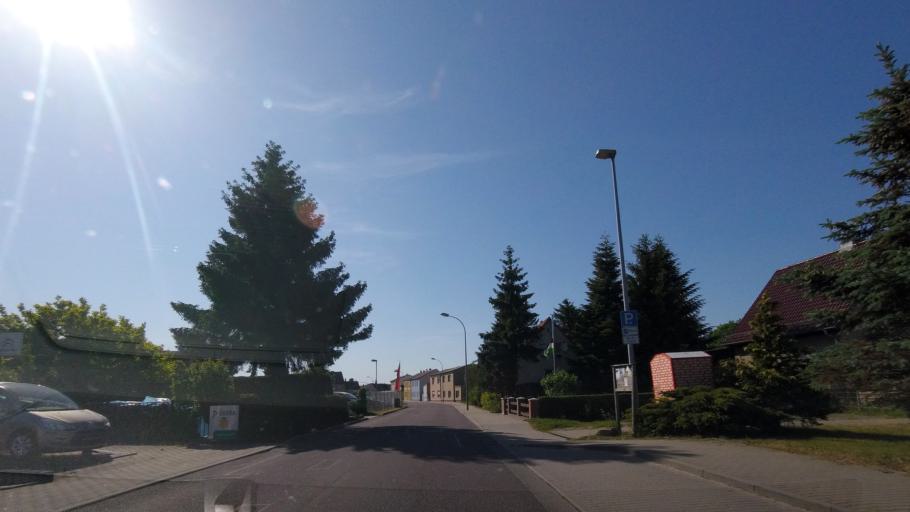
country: DE
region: Brandenburg
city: Brandenburg an der Havel
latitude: 52.3880
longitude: 12.5970
